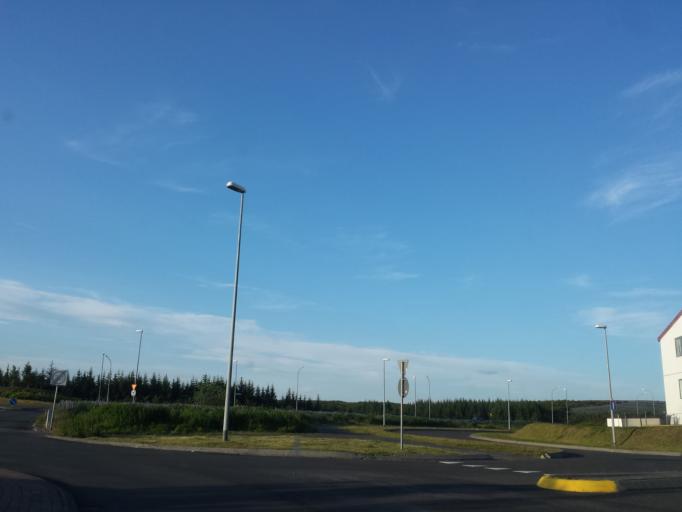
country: IS
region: Capital Region
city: Mosfellsbaer
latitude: 64.1014
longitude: -21.7647
